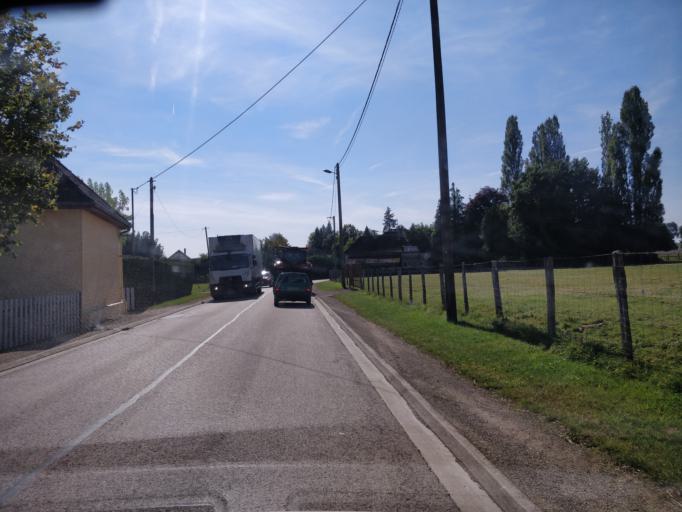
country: FR
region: Champagne-Ardenne
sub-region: Departement de l'Aube
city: Bouilly
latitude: 48.1230
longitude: 3.9658
